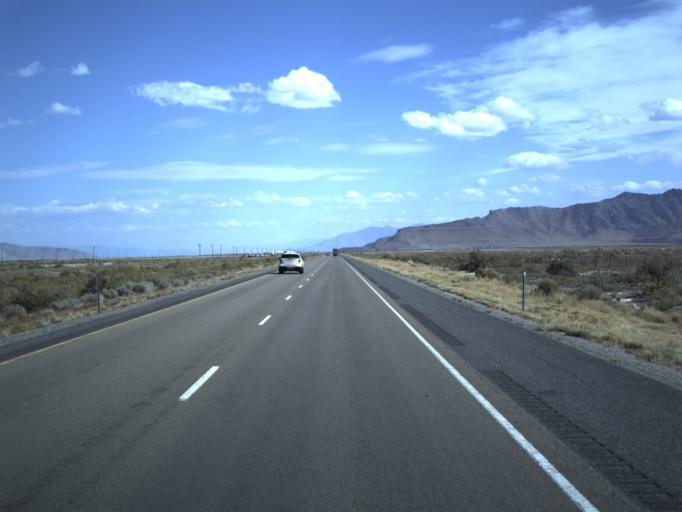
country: US
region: Utah
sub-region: Tooele County
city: Grantsville
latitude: 40.7545
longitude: -112.7414
